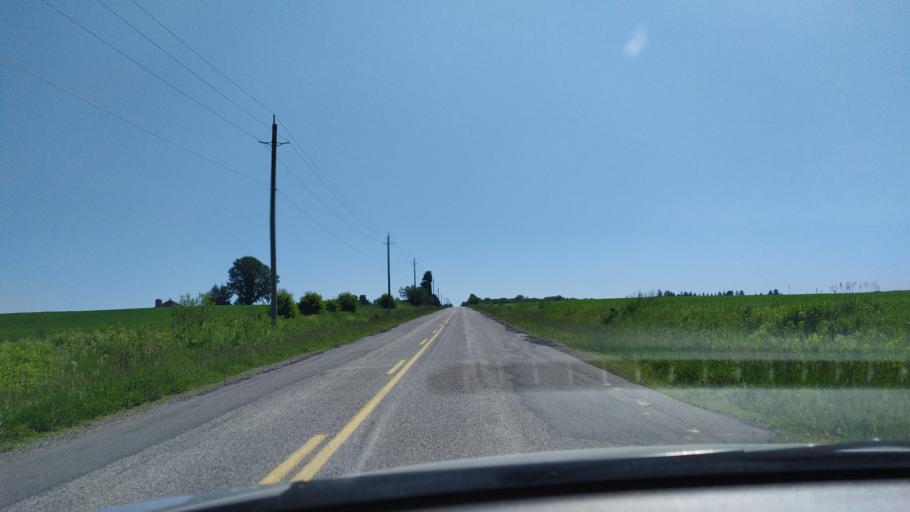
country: CA
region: Ontario
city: Waterloo
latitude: 43.4562
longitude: -80.7364
